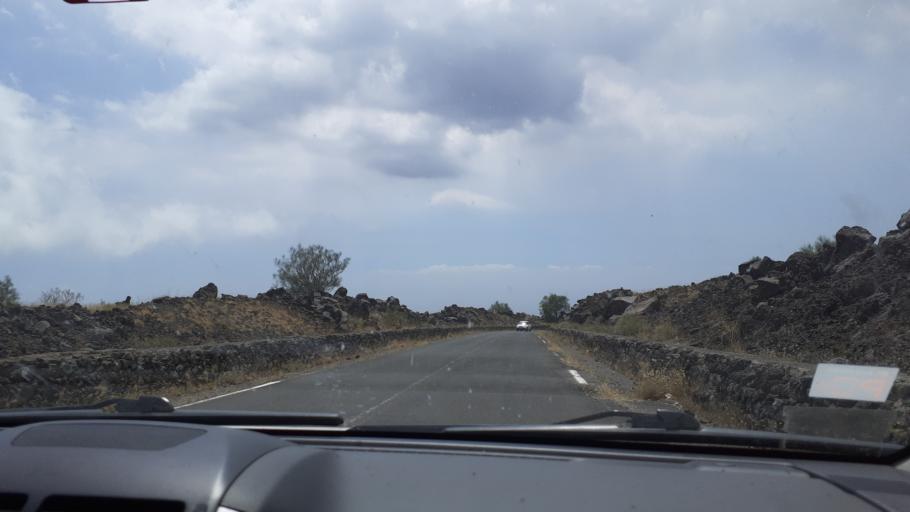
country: IT
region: Sicily
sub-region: Catania
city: Nicolosi
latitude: 37.6861
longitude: 15.0296
